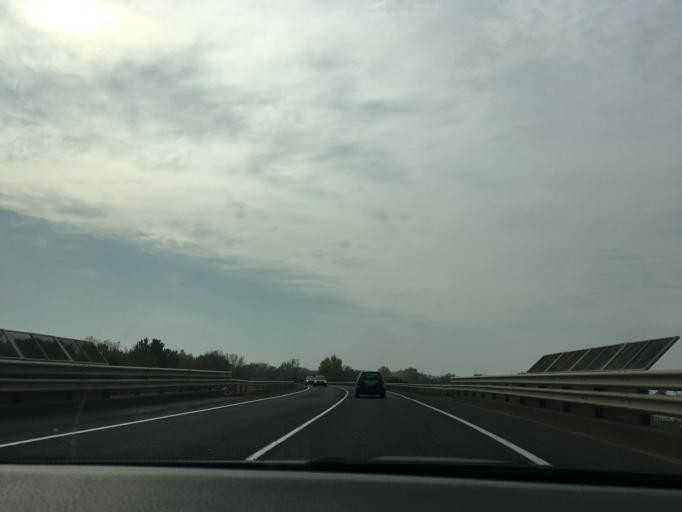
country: HU
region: Hajdu-Bihar
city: Debrecen
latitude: 47.5089
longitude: 21.5953
